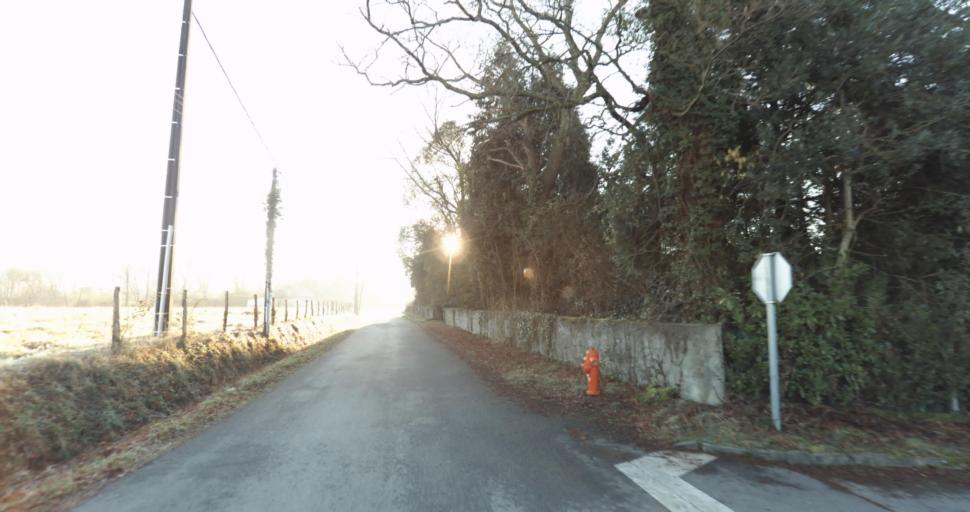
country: FR
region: Aquitaine
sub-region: Departement des Pyrenees-Atlantiques
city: Morlaas
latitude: 43.3288
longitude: -0.2656
